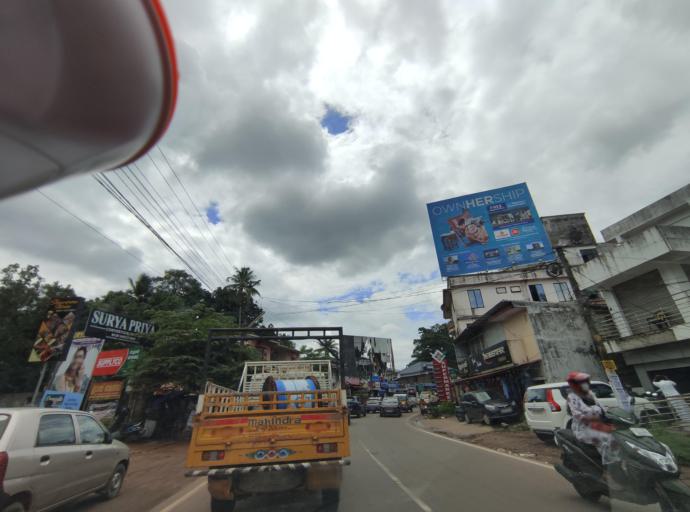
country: IN
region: Kerala
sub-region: Thiruvananthapuram
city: Nedumangad
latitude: 8.5930
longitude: 76.9524
